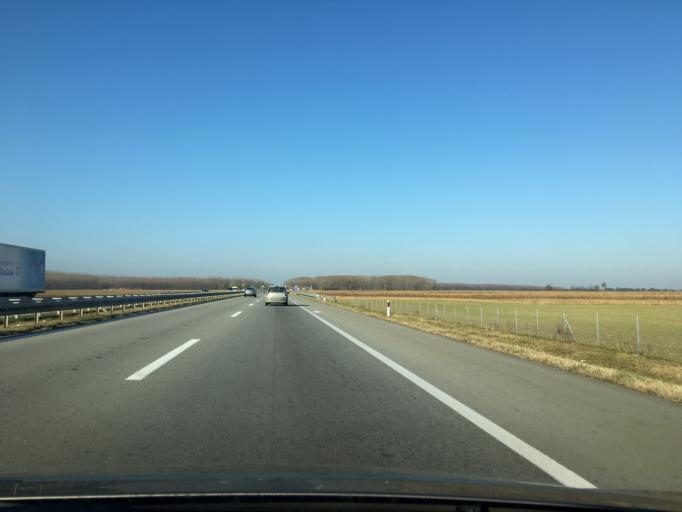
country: RS
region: Autonomna Pokrajina Vojvodina
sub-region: Juznobacki Okrug
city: Petrovaradin
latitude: 45.2727
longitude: 19.9377
